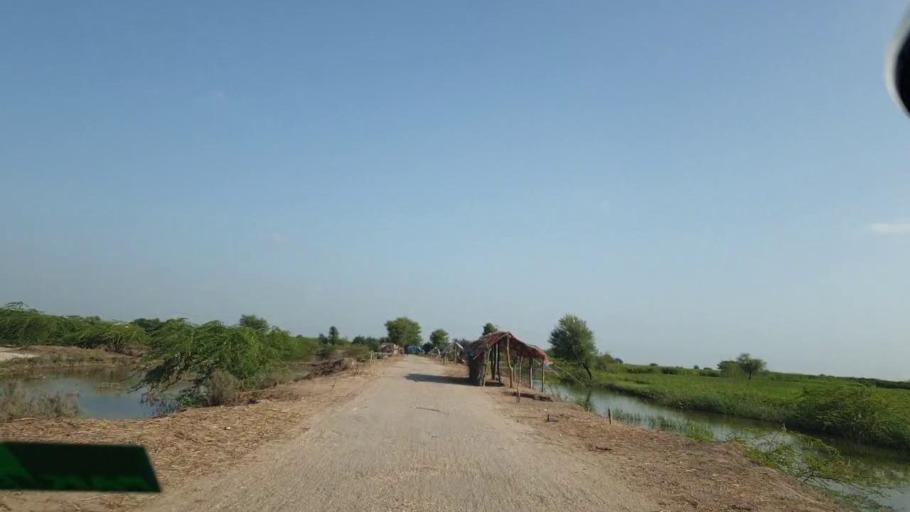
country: PK
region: Sindh
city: Naukot
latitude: 24.7391
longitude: 69.2070
